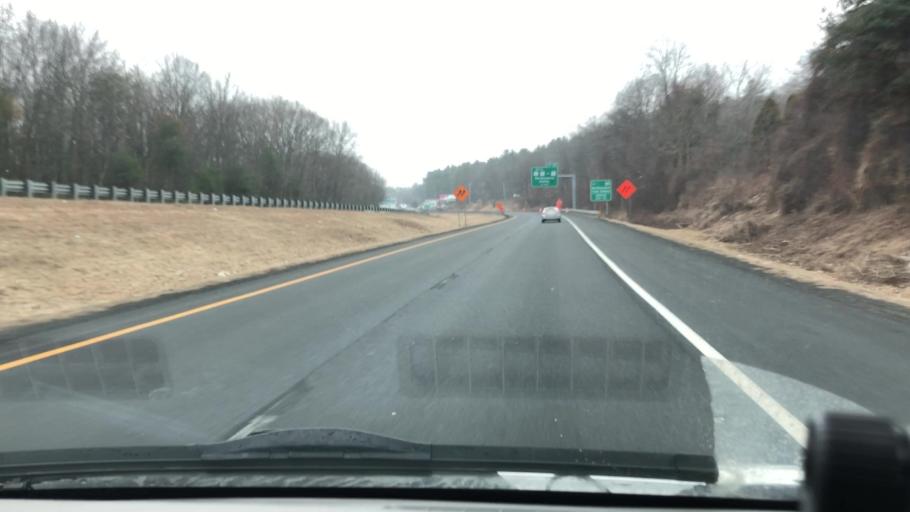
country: US
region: Massachusetts
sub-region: Hampshire County
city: Northampton
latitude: 42.3509
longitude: -72.6409
